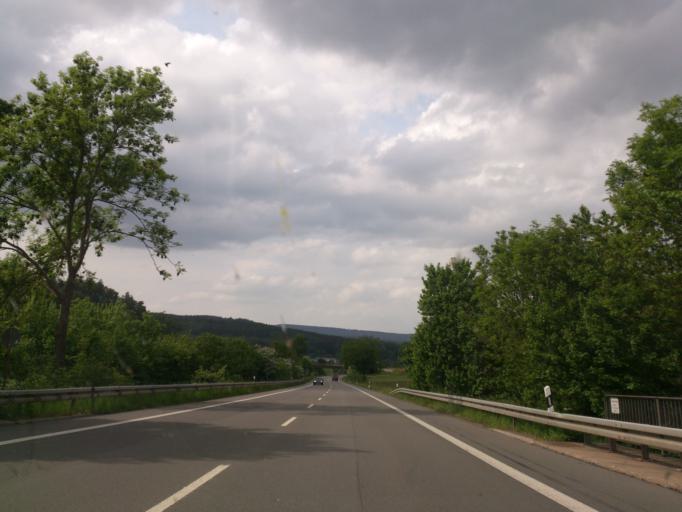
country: DE
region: North Rhine-Westphalia
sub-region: Regierungsbezirk Detmold
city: Willebadessen
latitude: 51.5057
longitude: 9.0159
